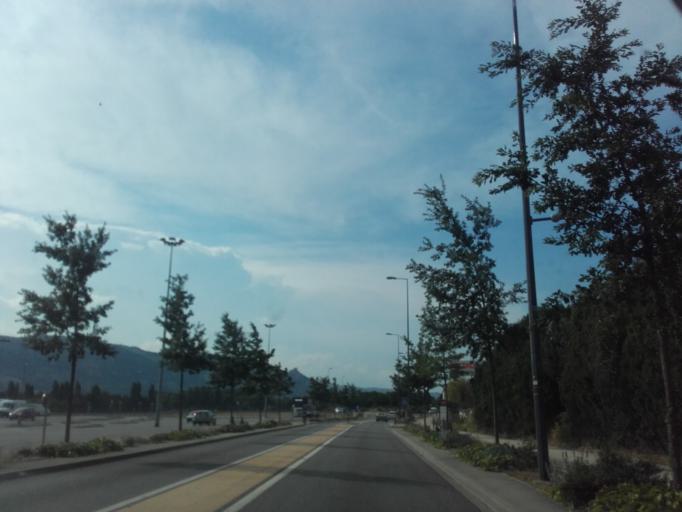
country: FR
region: Rhone-Alpes
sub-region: Departement de l'Ardeche
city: Guilherand-Granges
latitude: 44.9085
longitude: 4.8795
